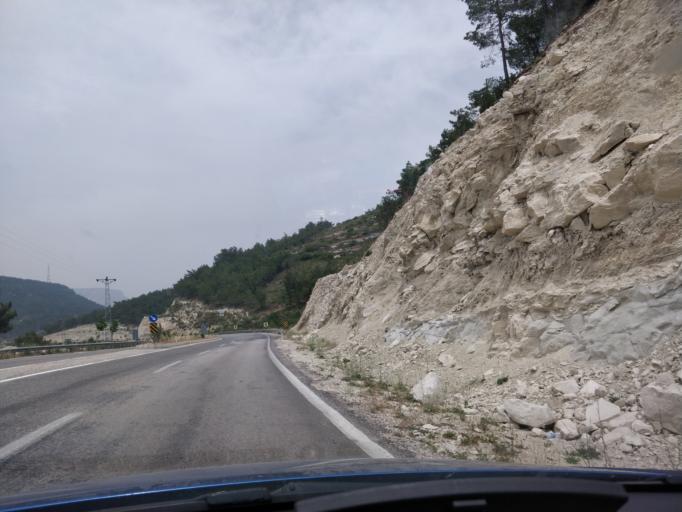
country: TR
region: Mersin
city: Tasucu
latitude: 36.3935
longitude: 33.8417
